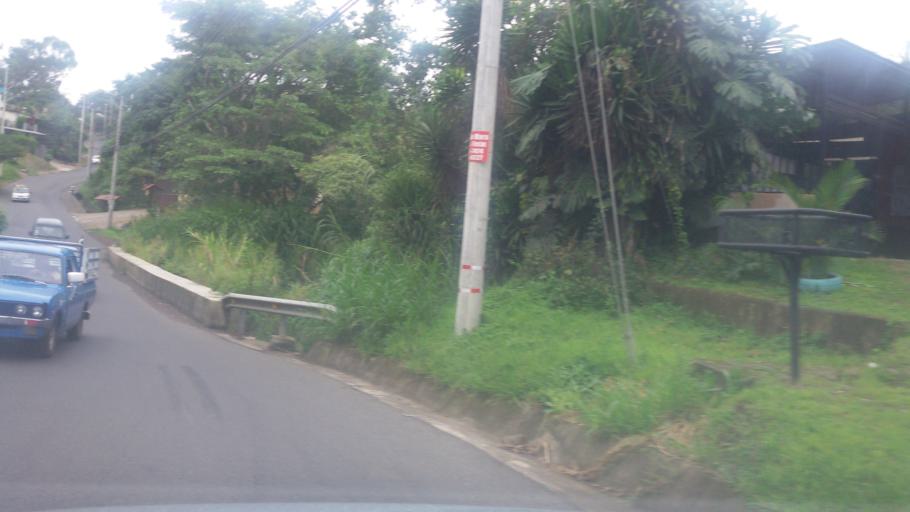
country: CR
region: Heredia
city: Angeles
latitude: 9.9857
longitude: -84.0576
